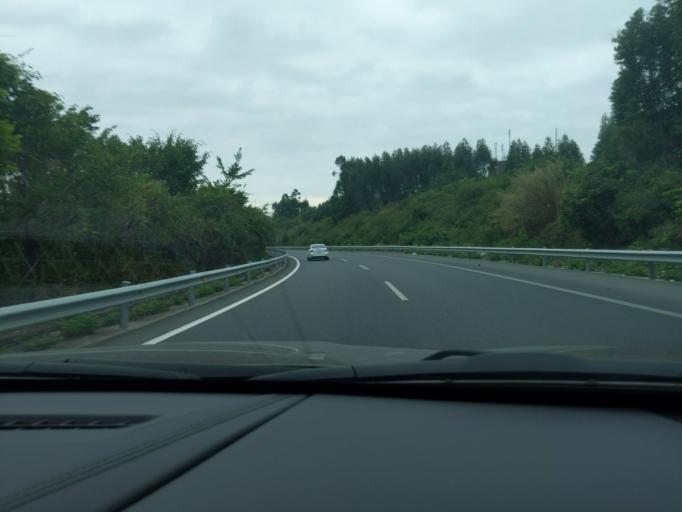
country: CN
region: Fujian
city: Neikeng
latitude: 24.7873
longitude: 118.4756
